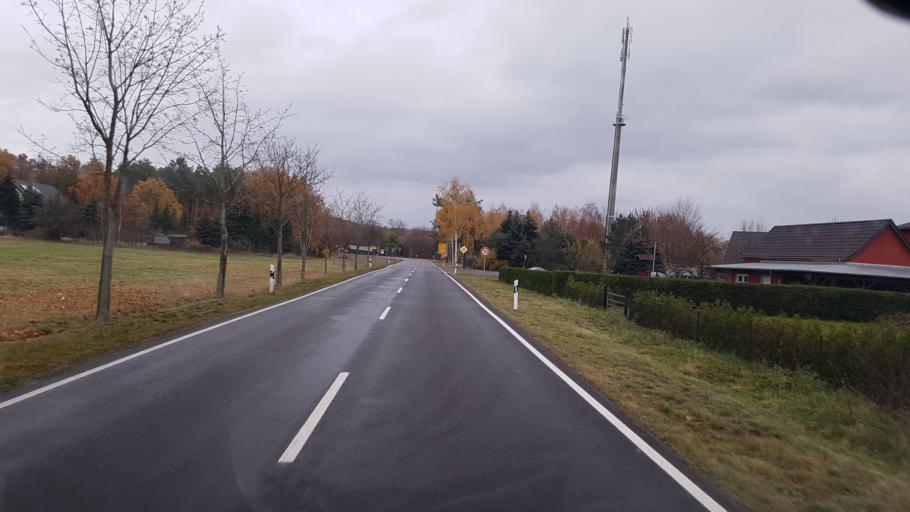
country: DE
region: Brandenburg
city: Ortrand
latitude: 51.3814
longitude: 13.7655
